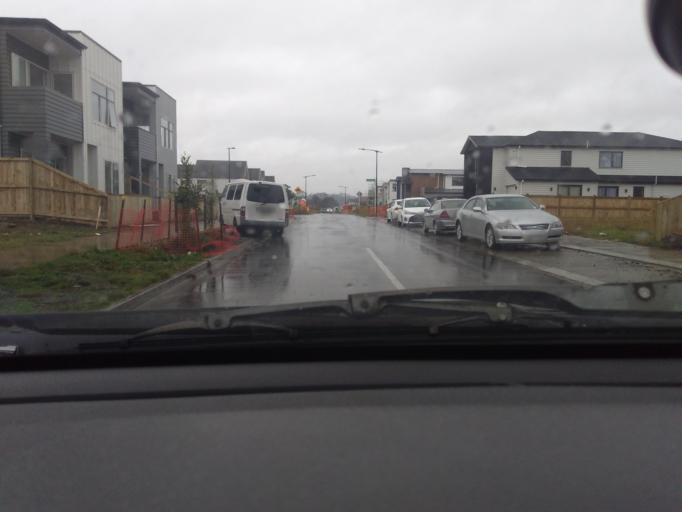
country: NZ
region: Auckland
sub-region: Auckland
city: Rosebank
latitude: -36.8049
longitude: 174.6637
